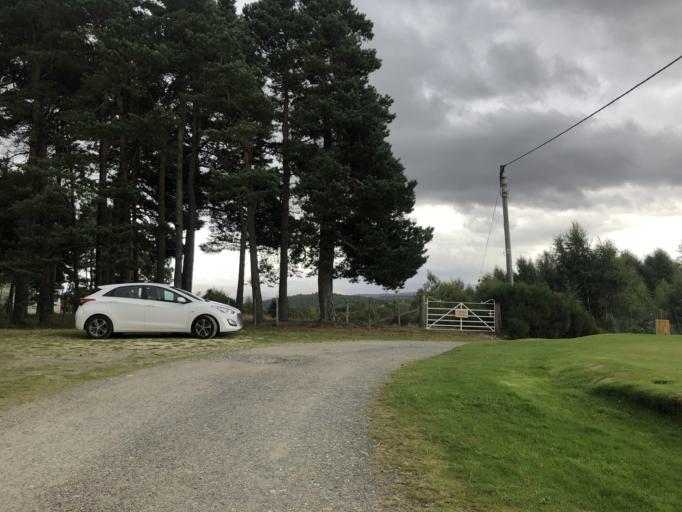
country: GB
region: Scotland
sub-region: Highland
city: Kingussie
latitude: 57.0656
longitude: -4.1117
